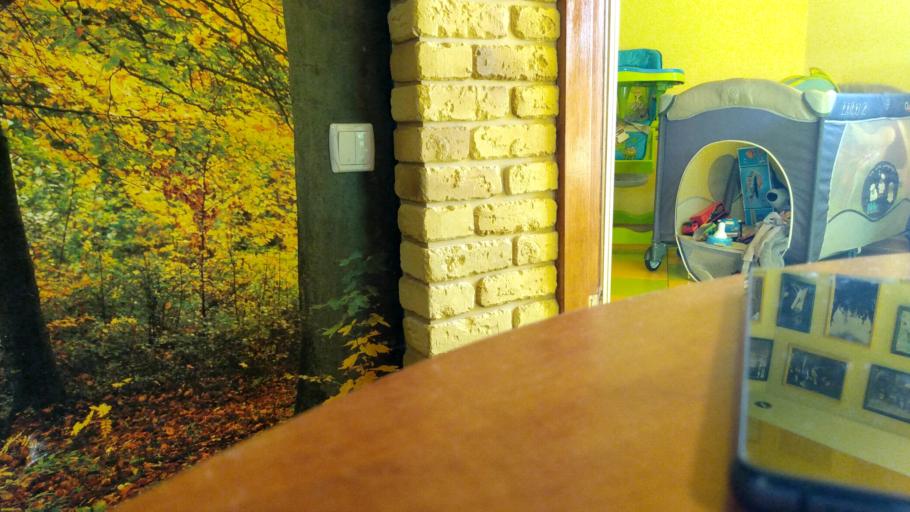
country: RU
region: Tverskaya
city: Likhoslavl'
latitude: 57.2164
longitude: 35.4890
